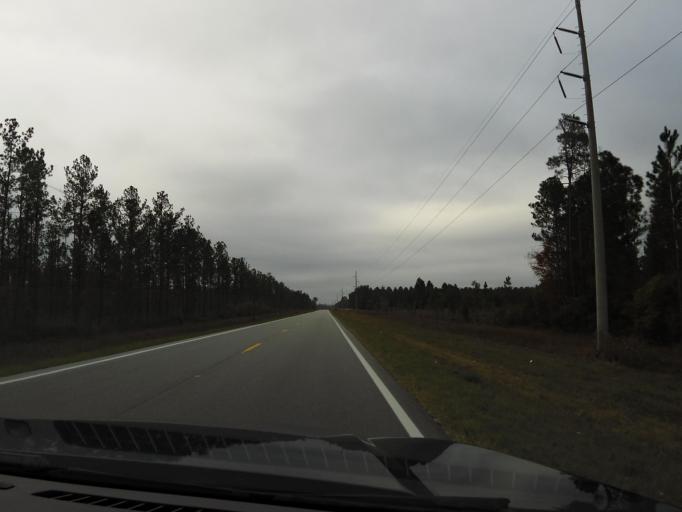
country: US
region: Georgia
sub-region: Charlton County
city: Folkston
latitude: 30.7427
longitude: -82.0712
